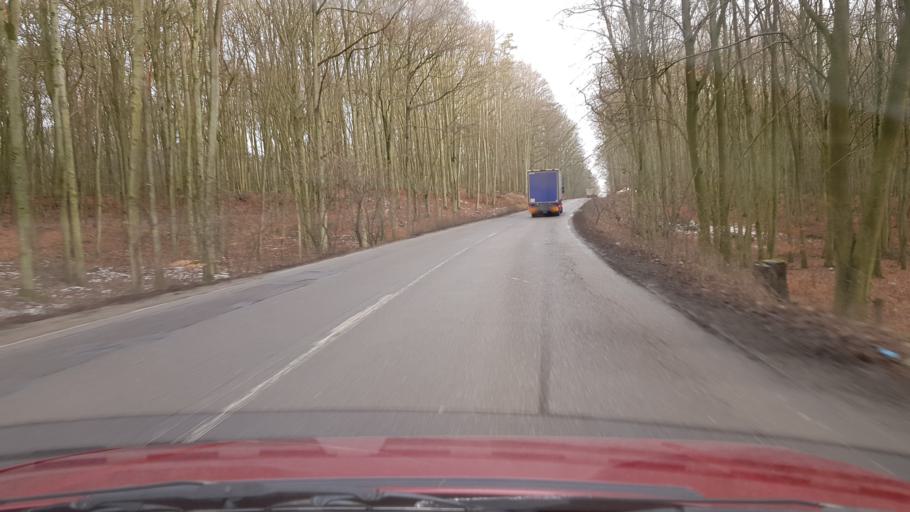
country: PL
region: West Pomeranian Voivodeship
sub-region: Powiat policki
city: Police
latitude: 53.5243
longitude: 14.5687
